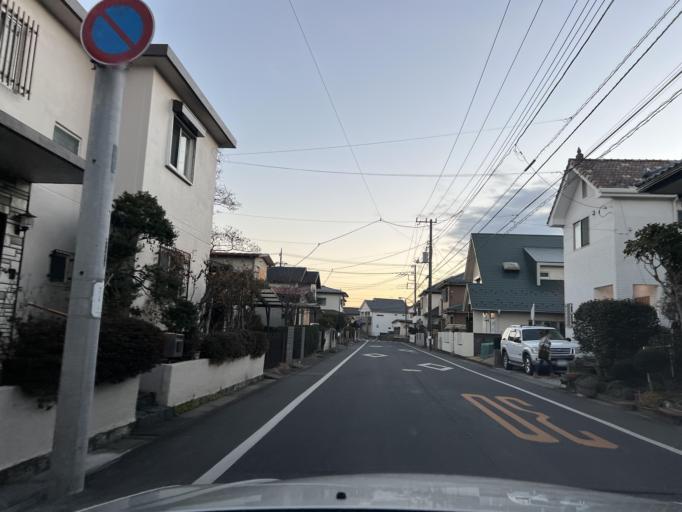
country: JP
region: Chiba
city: Nagareyama
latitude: 35.8846
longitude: 139.9303
